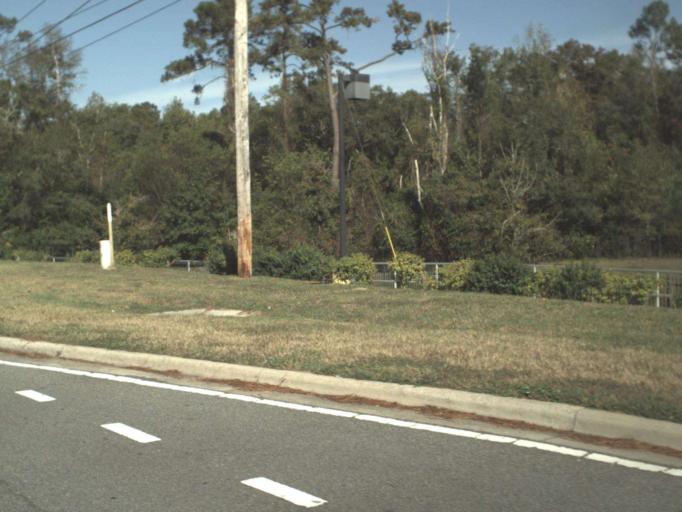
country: US
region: Florida
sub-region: Leon County
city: Tallahassee
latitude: 30.4884
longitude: -84.3196
